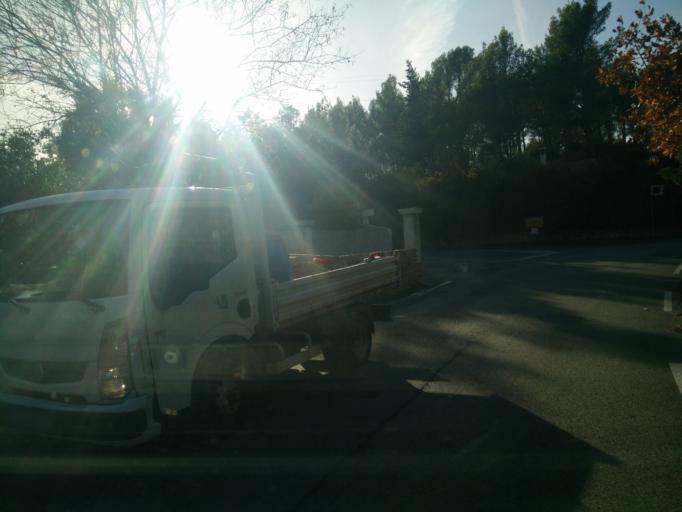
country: FR
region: Provence-Alpes-Cote d'Azur
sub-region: Departement du Var
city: Sollies-Toucas
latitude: 43.2027
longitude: 6.0047
